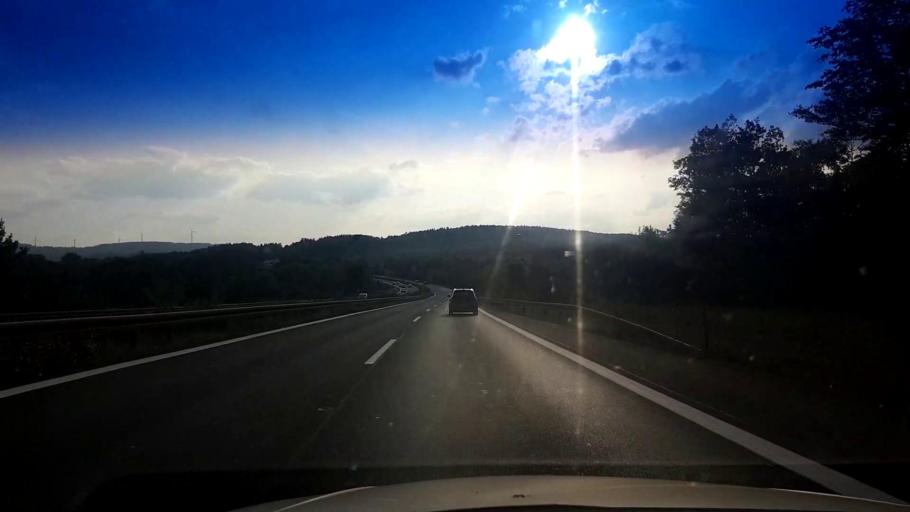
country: DE
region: Bavaria
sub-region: Upper Franconia
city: Neudrossenfeld
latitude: 50.0310
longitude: 11.4668
